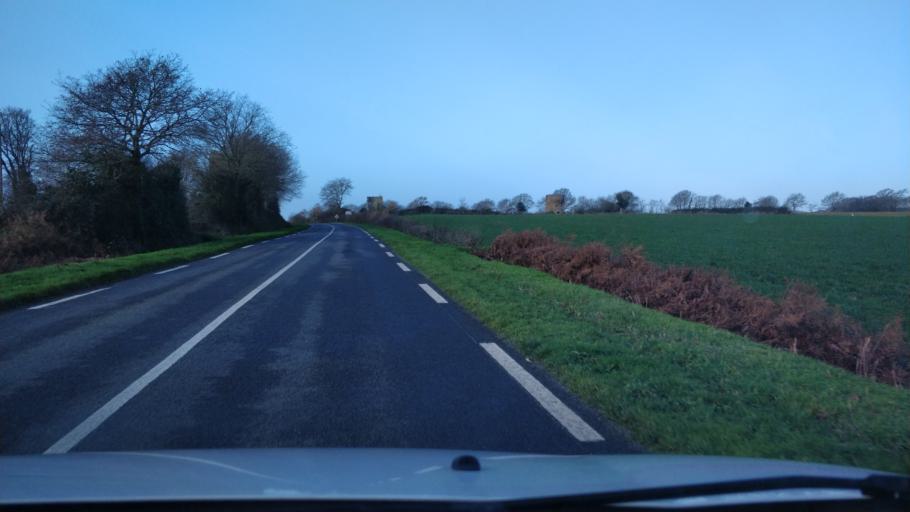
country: FR
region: Pays de la Loire
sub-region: Departement de la Loire-Atlantique
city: Asserac
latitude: 47.4303
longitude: -2.3753
